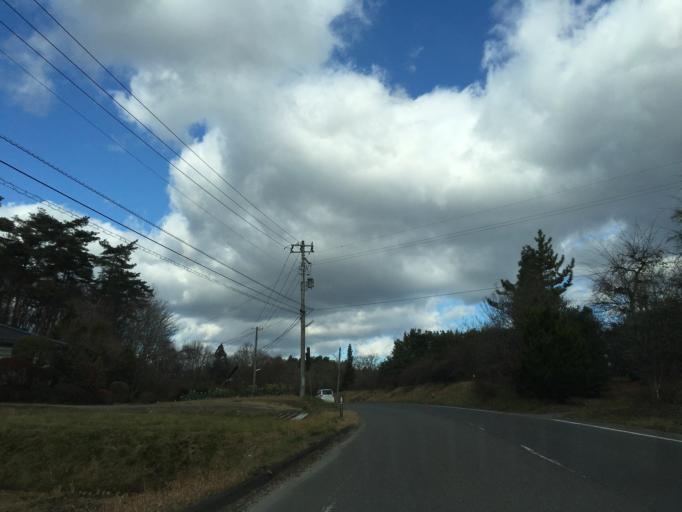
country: JP
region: Fukushima
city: Koriyama
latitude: 37.3554
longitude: 140.4473
